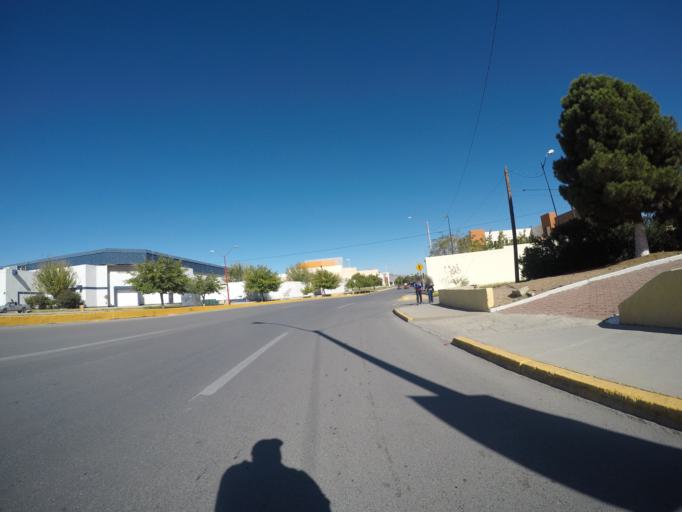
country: MX
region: Chihuahua
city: Ciudad Juarez
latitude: 31.7416
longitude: -106.4437
